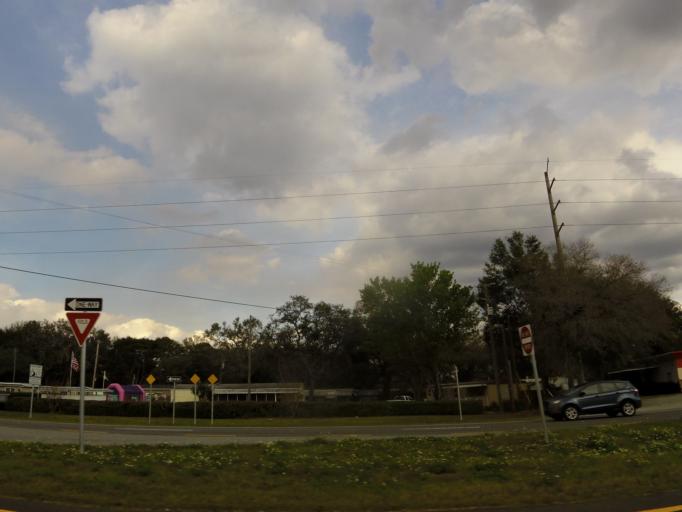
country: US
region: Florida
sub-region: Volusia County
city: De Leon Springs
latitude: 29.0908
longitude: -81.3288
